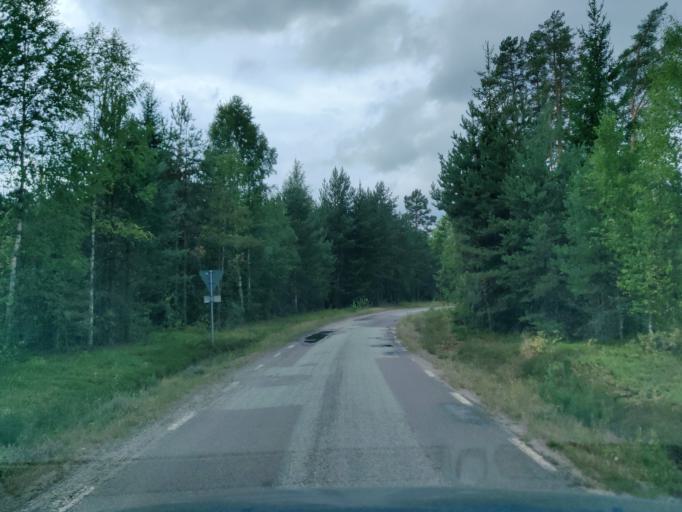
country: SE
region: Vaermland
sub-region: Munkfors Kommun
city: Munkfors
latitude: 59.9253
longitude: 13.5727
